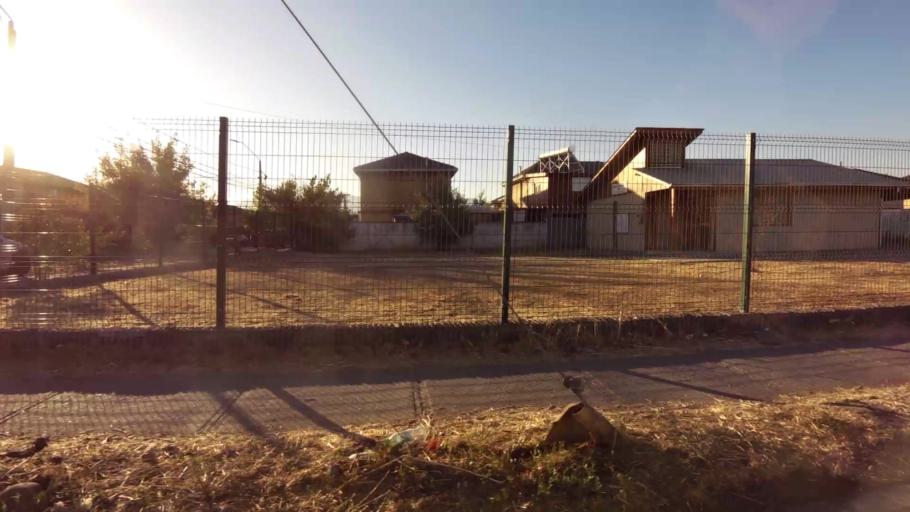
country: CL
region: O'Higgins
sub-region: Provincia de Cachapoal
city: Rancagua
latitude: -34.1763
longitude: -70.7576
